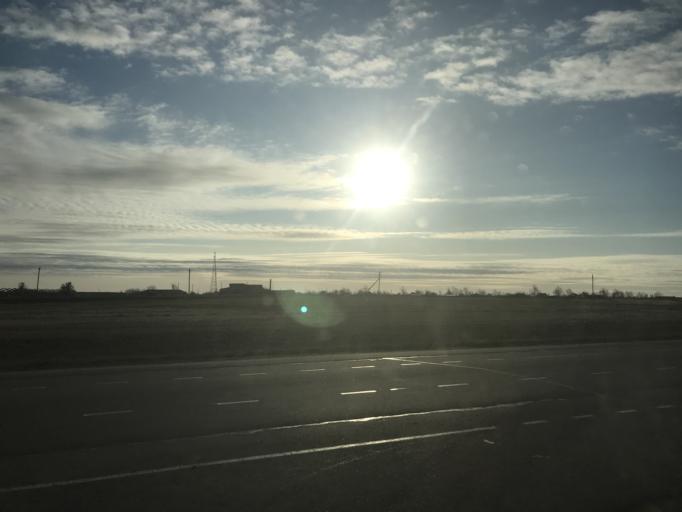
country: KZ
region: Qostanay
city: Ordzhonikidze
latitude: 52.0994
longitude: 61.9881
